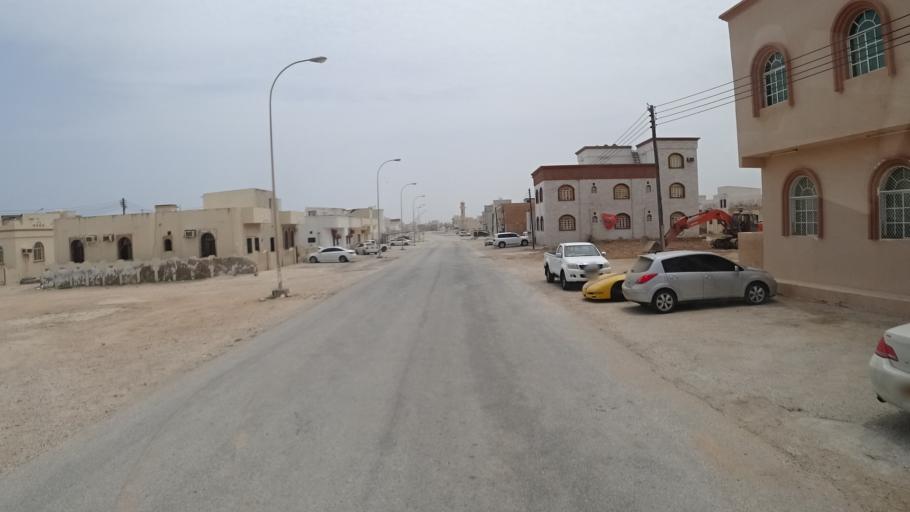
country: OM
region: Zufar
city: Salalah
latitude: 17.0370
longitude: 54.4079
